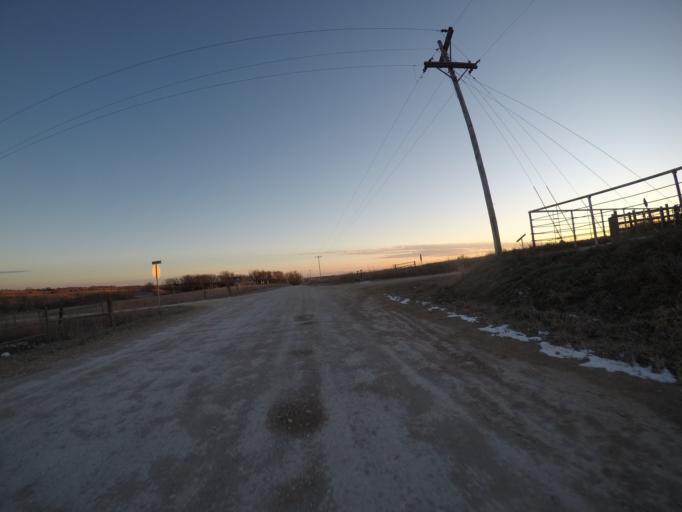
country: US
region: Kansas
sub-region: Riley County
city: Manhattan
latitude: 39.2623
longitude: -96.4827
